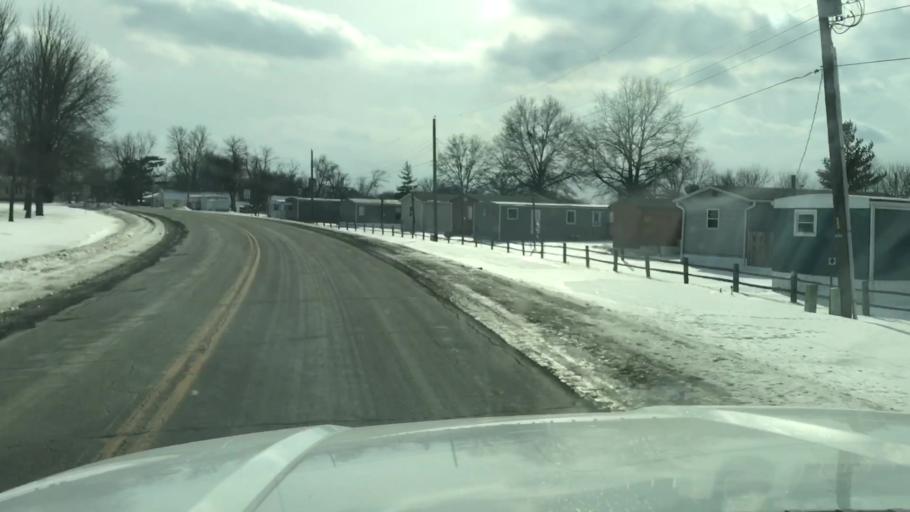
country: US
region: Missouri
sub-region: Gentry County
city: Stanberry
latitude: 40.3569
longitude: -94.6728
